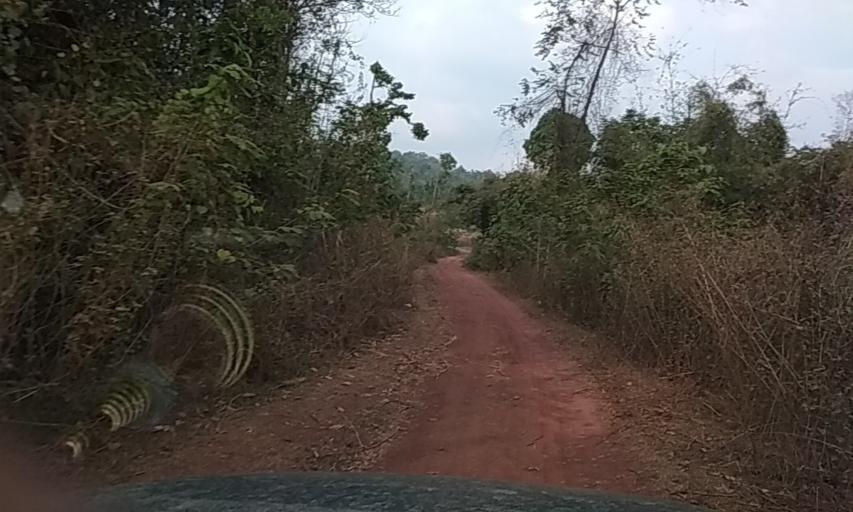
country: TH
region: Nan
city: Mae Charim
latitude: 18.4483
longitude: 101.1952
